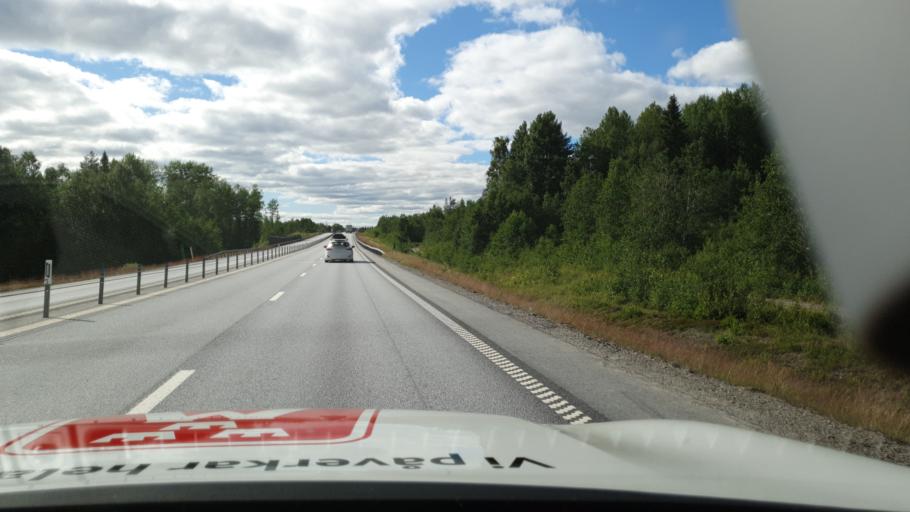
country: SE
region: Vaesterbotten
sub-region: Vannas Kommun
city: Vannasby
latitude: 63.8975
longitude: 19.9175
